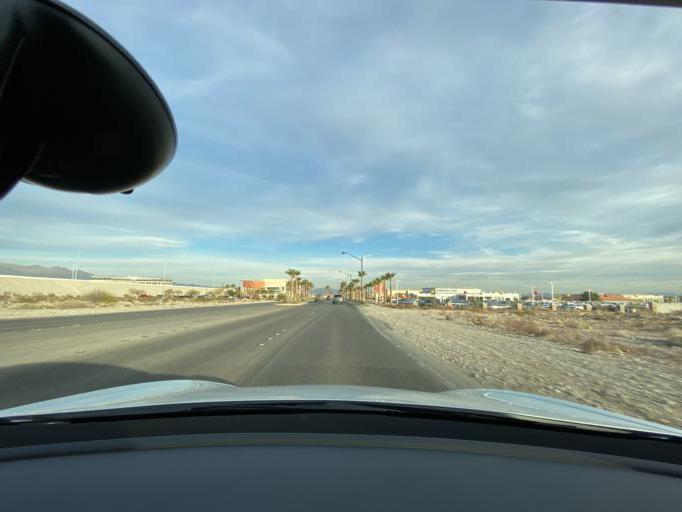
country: US
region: Nevada
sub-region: Clark County
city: Summerlin South
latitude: 36.2772
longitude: -115.2849
